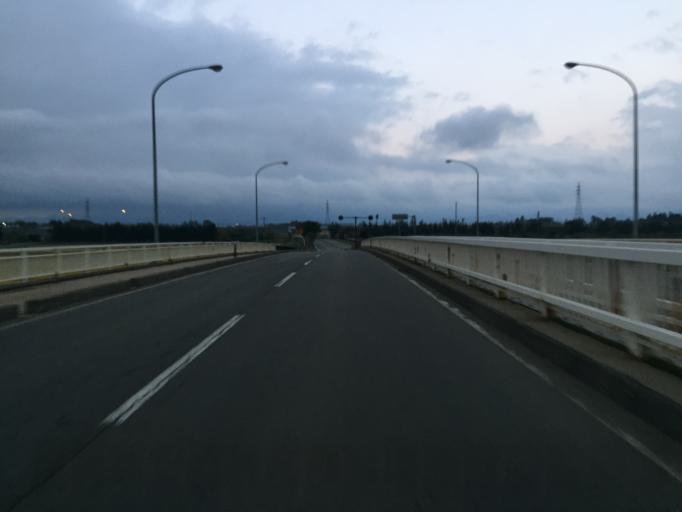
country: JP
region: Fukushima
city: Inawashiro
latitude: 37.5452
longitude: 140.1111
